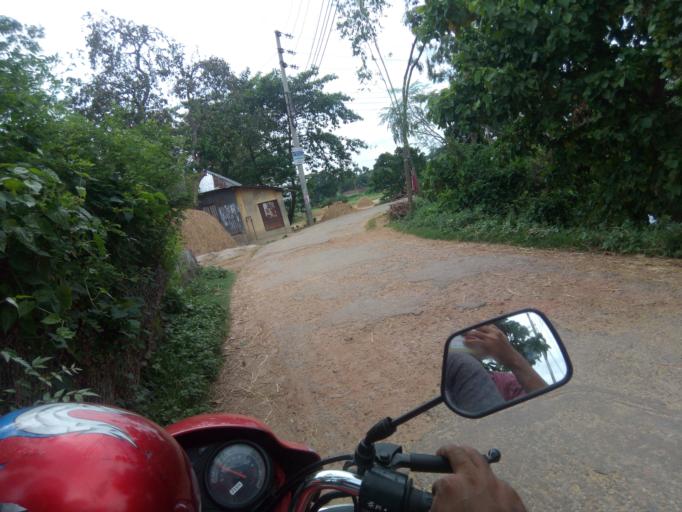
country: BD
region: Dhaka
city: Paltan
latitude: 23.7438
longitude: 90.4897
